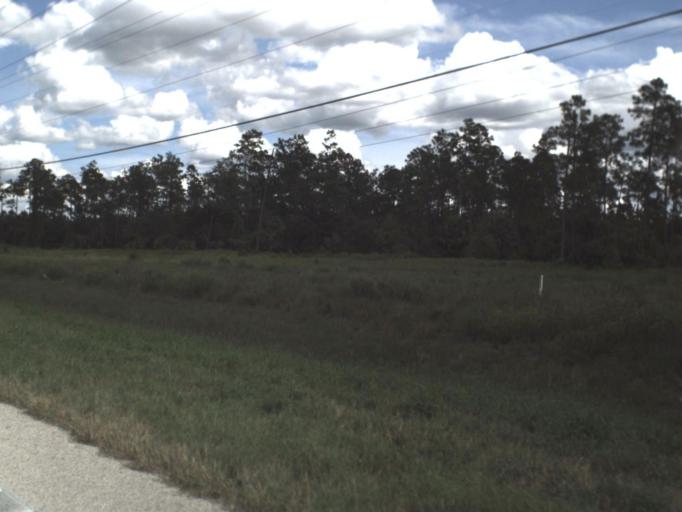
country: US
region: Florida
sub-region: Polk County
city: Mulberry
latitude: 27.8951
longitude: -81.9149
